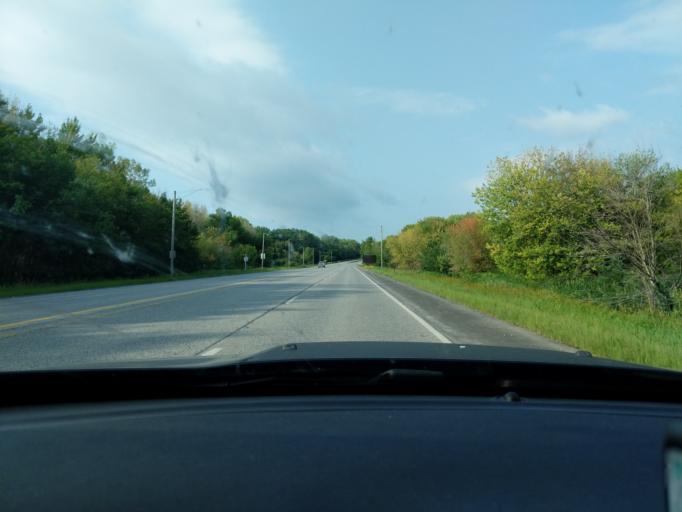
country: US
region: Illinois
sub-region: Rock Island County
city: Rock Island
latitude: 41.5051
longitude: -90.6142
